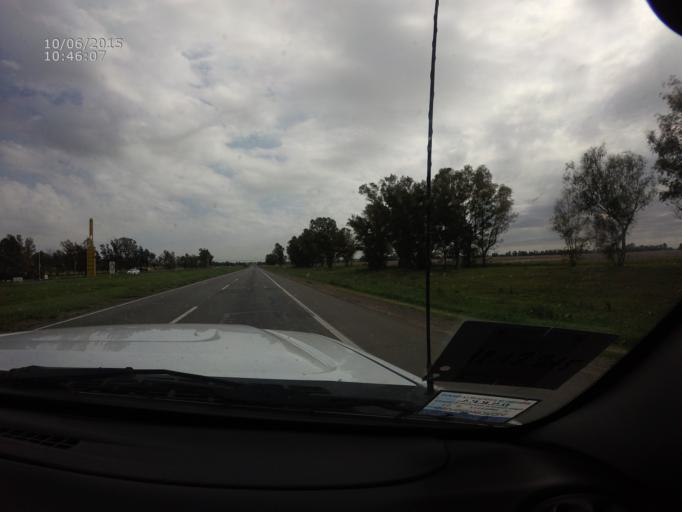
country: AR
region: Buenos Aires
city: San Nicolas de los Arroyos
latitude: -33.4219
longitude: -60.1788
